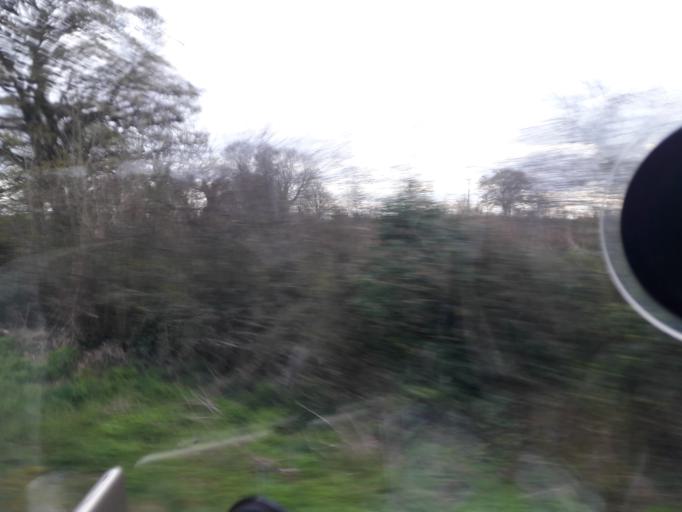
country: IE
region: Leinster
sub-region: An Iarmhi
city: An Muileann gCearr
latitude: 53.5900
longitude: -7.3861
